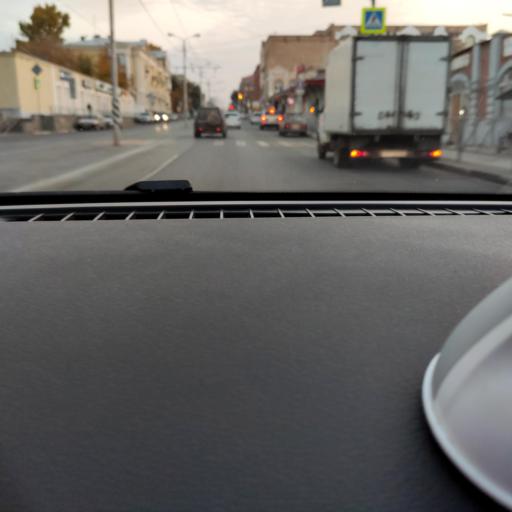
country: RU
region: Samara
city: Samara
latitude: 53.1843
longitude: 50.0971
